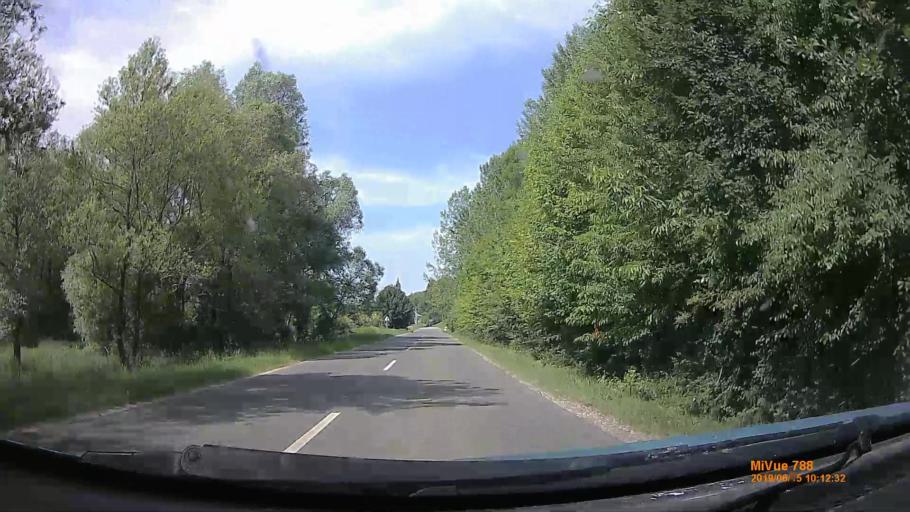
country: HU
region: Baranya
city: Buekkoesd
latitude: 46.1384
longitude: 18.0517
